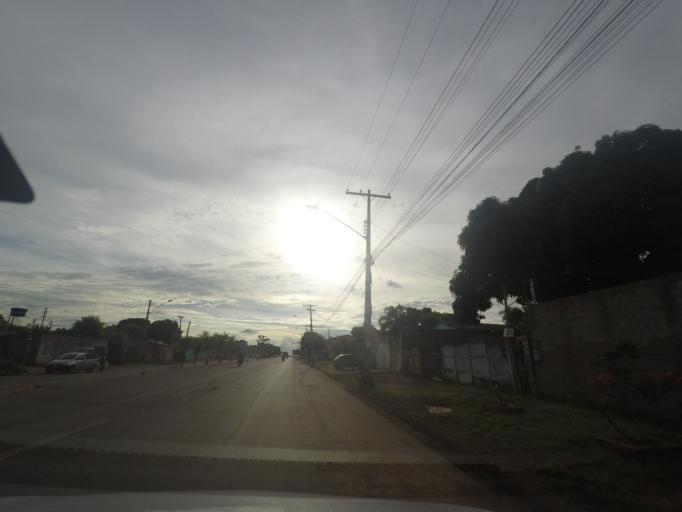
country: BR
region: Goias
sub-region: Goiania
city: Goiania
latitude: -16.6847
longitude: -49.3534
